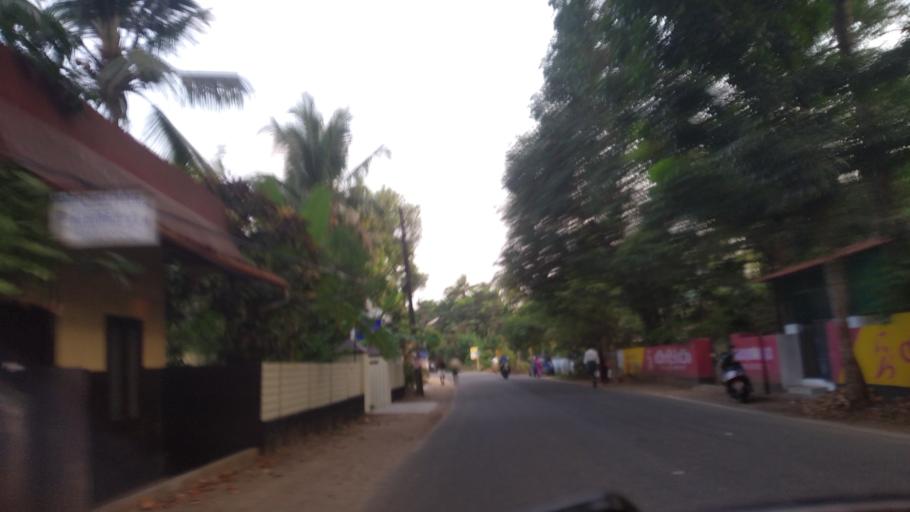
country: IN
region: Kerala
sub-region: Thrissur District
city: Kodungallur
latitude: 10.2344
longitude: 76.1535
